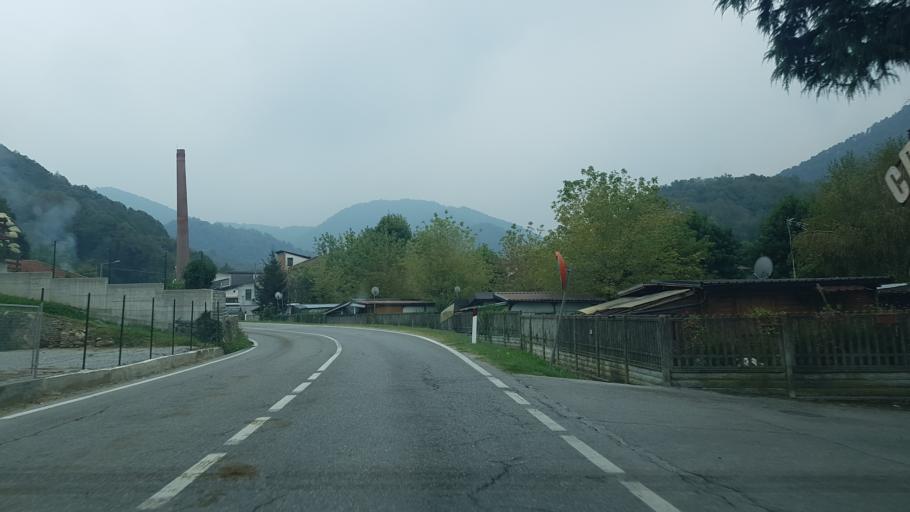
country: IT
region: Piedmont
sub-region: Provincia di Cuneo
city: Frabosa Sottana
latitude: 44.3248
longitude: 7.8002
